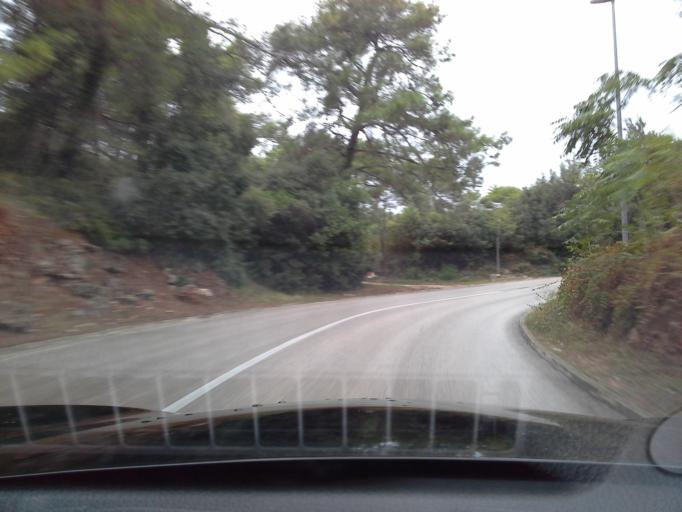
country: HR
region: Primorsko-Goranska
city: Mali Losinj
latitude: 44.5196
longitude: 14.4974
